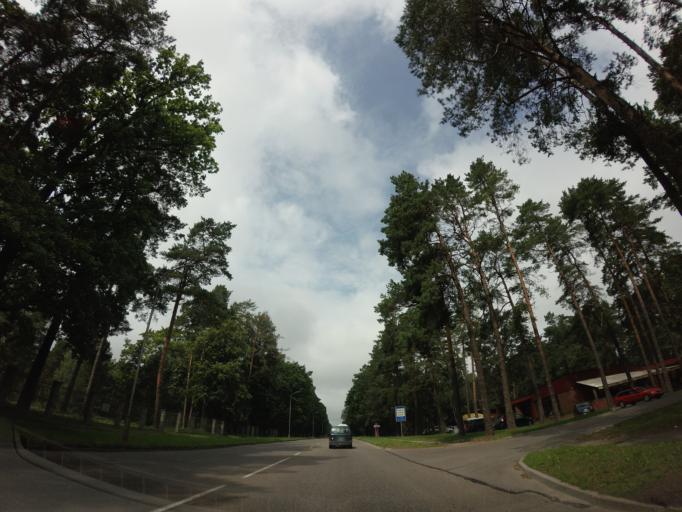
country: LT
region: Alytaus apskritis
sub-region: Alytus
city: Alytus
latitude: 54.3798
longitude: 24.0623
